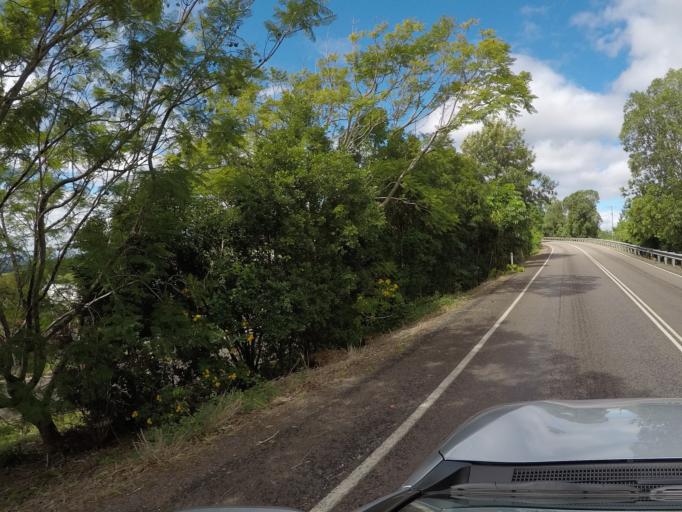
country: AU
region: Queensland
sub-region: Sunshine Coast
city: Nambour
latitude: -26.6363
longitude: 152.8697
